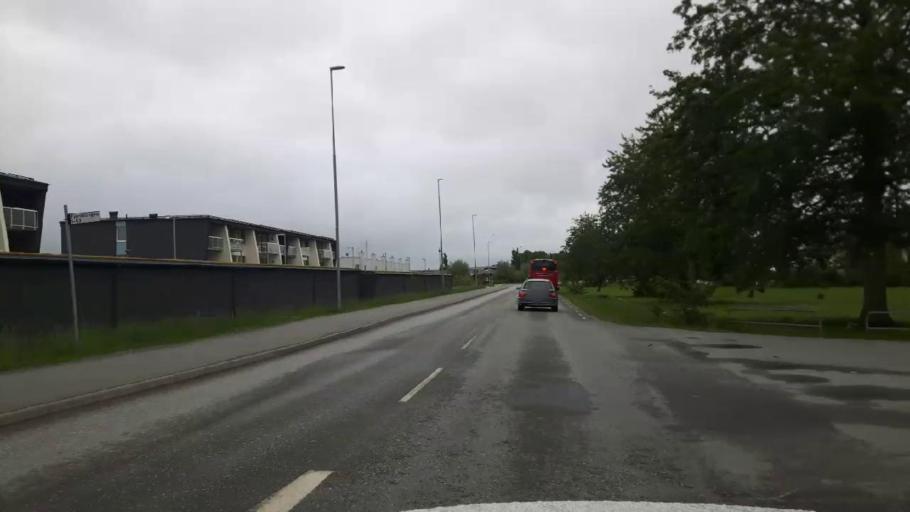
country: SE
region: Stockholm
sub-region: Upplands-Bro Kommun
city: Bro
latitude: 59.5135
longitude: 17.6560
